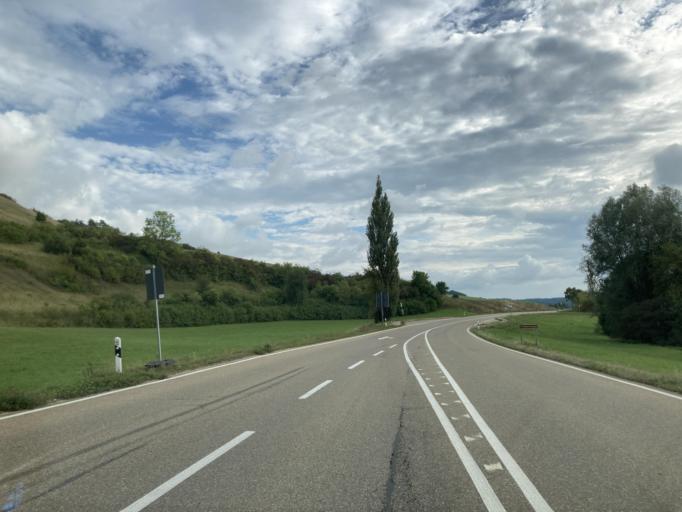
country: DE
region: Baden-Wuerttemberg
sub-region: Regierungsbezirk Stuttgart
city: Dischingen
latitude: 48.7147
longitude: 10.3807
